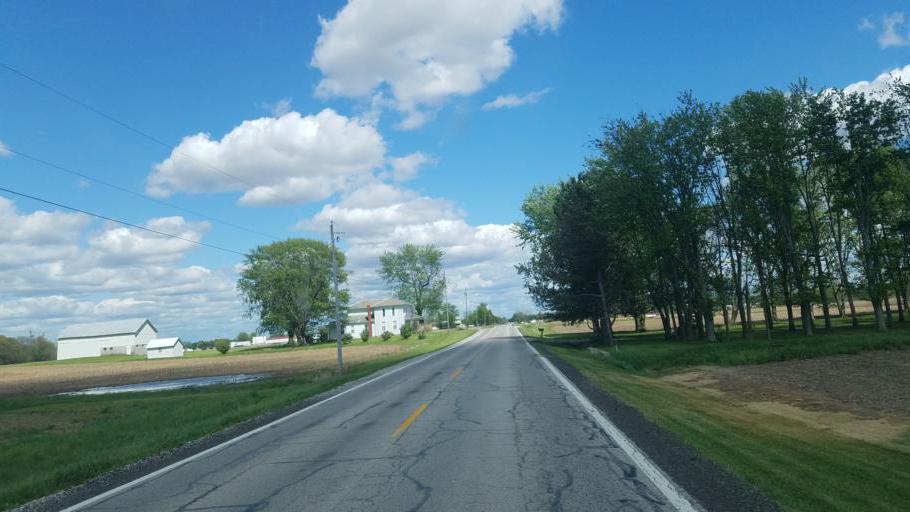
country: US
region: Ohio
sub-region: Marion County
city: Prospect
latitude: 40.4514
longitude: -83.1045
